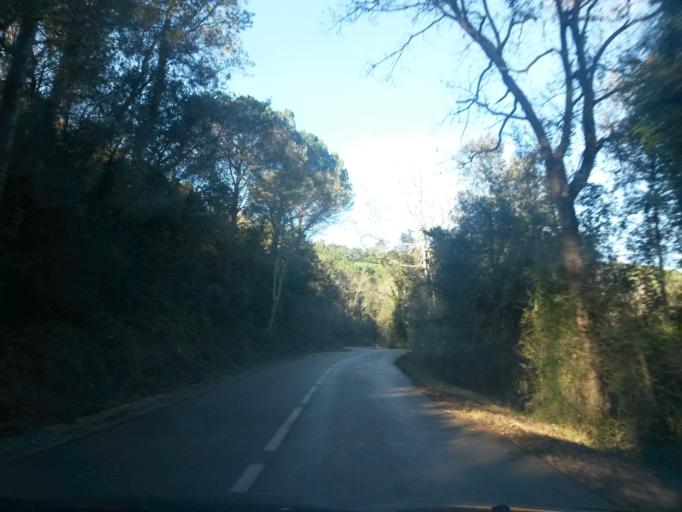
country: ES
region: Catalonia
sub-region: Provincia de Girona
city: Angles
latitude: 41.9970
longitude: 2.6698
